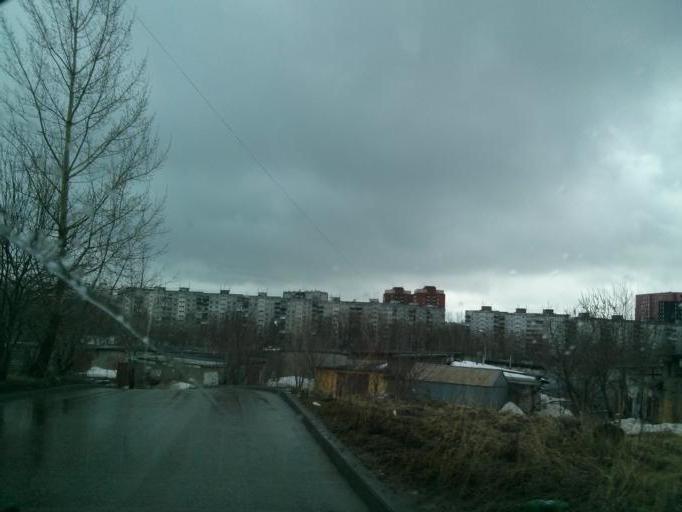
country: RU
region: Nizjnij Novgorod
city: Afonino
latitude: 56.3024
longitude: 44.0662
